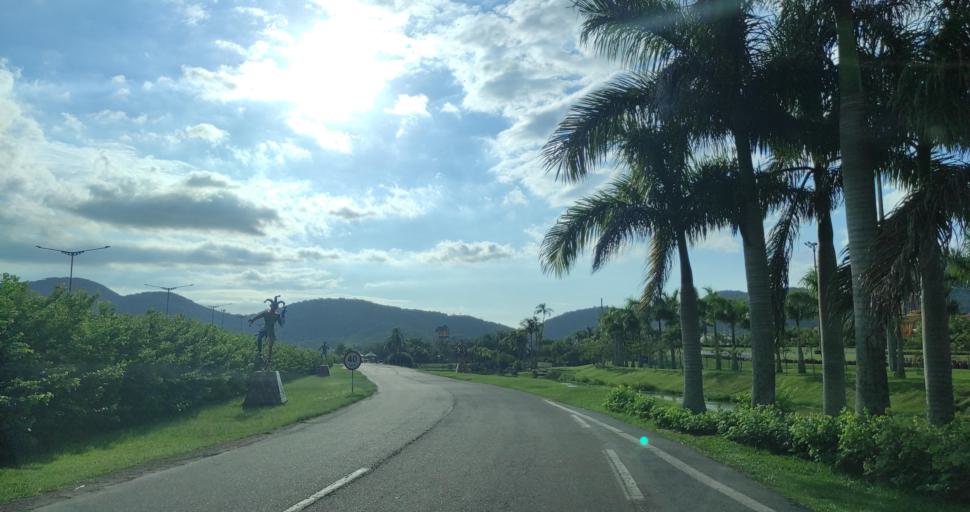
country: BR
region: Santa Catarina
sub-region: Penha
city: Penha
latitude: -26.7982
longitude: -48.6201
